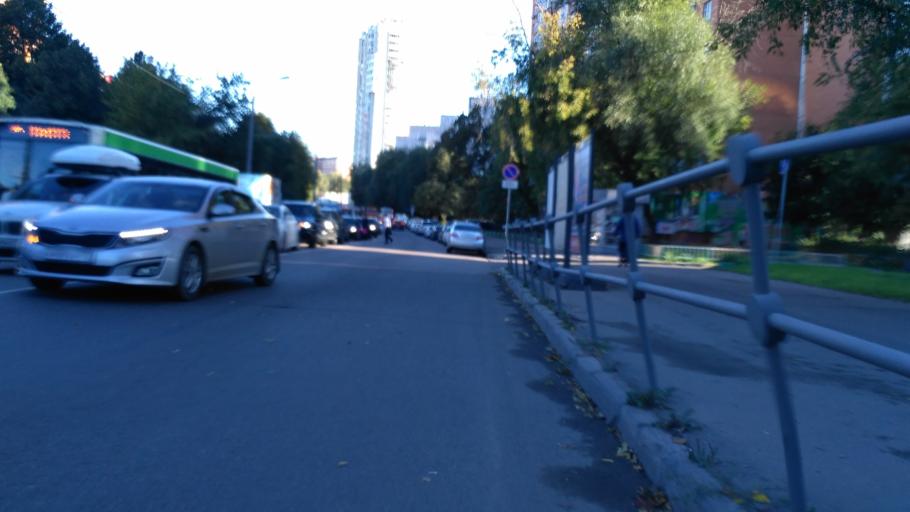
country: RU
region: Moscow
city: Likhobory
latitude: 55.8580
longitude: 37.5625
